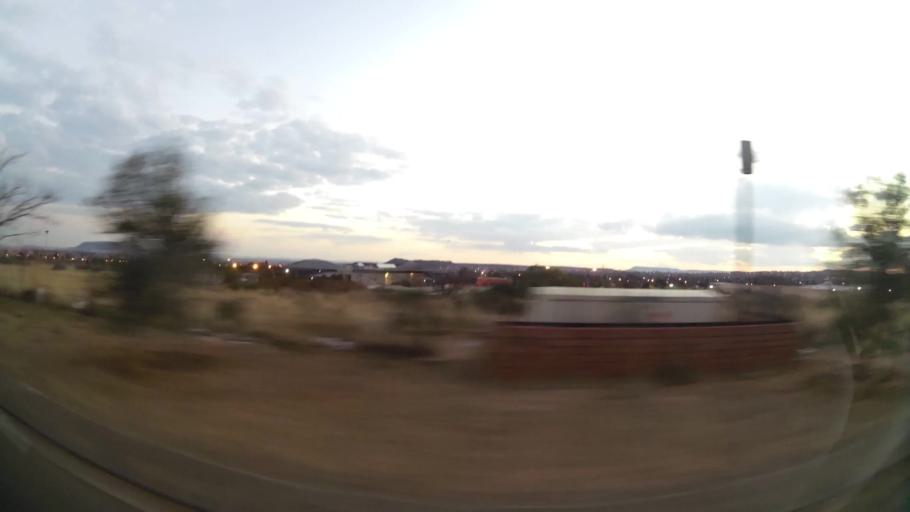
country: ZA
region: Orange Free State
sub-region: Mangaung Metropolitan Municipality
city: Bloemfontein
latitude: -29.1591
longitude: 26.1935
